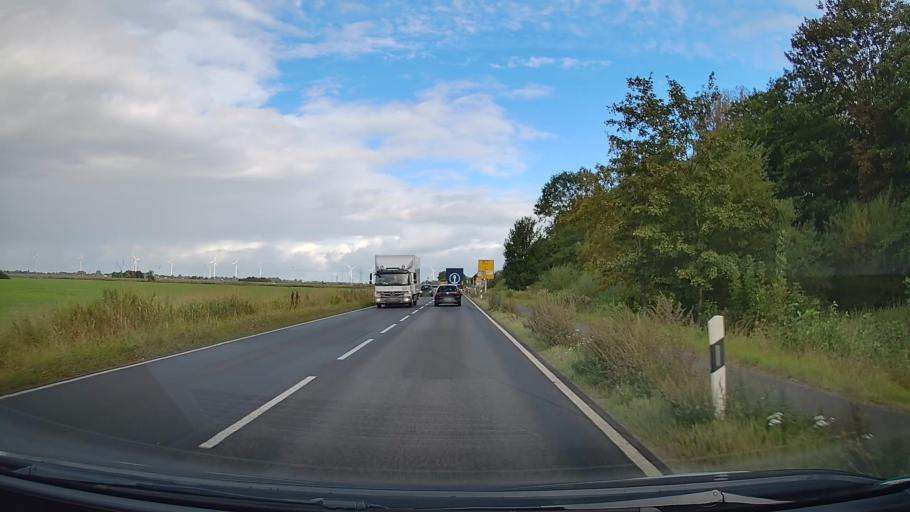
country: DE
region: Lower Saxony
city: Brake (Unterweser)
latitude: 53.3284
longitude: 8.4589
